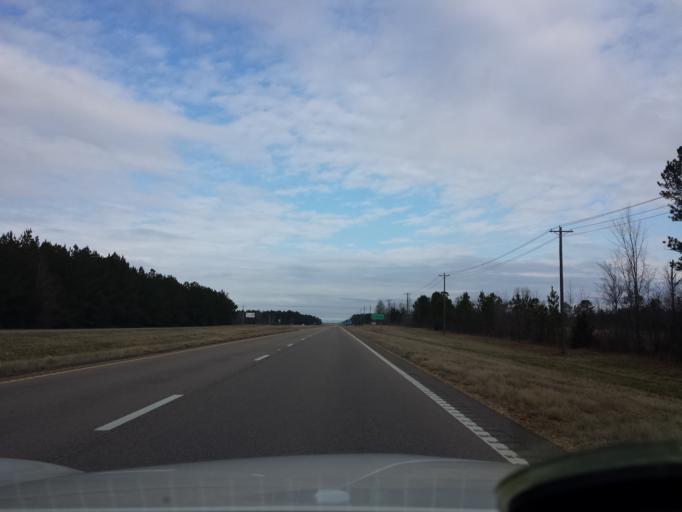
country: US
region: Mississippi
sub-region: Oktibbeha County
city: Starkville
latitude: 33.4166
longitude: -88.8538
